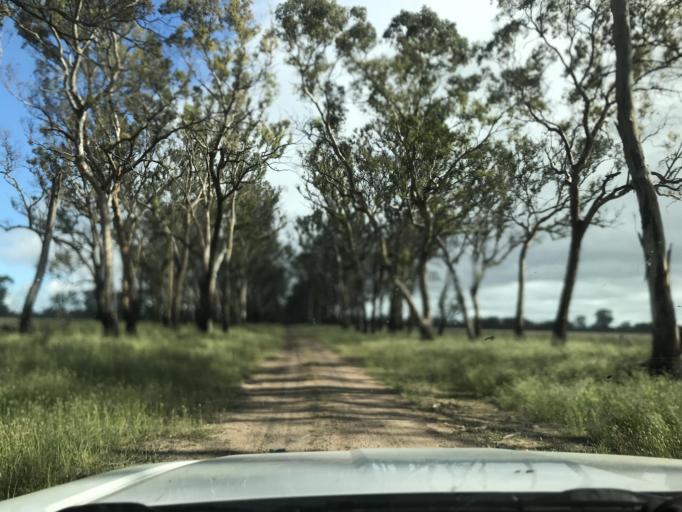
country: AU
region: South Australia
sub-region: Wattle Range
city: Penola
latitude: -37.2002
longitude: 141.1275
